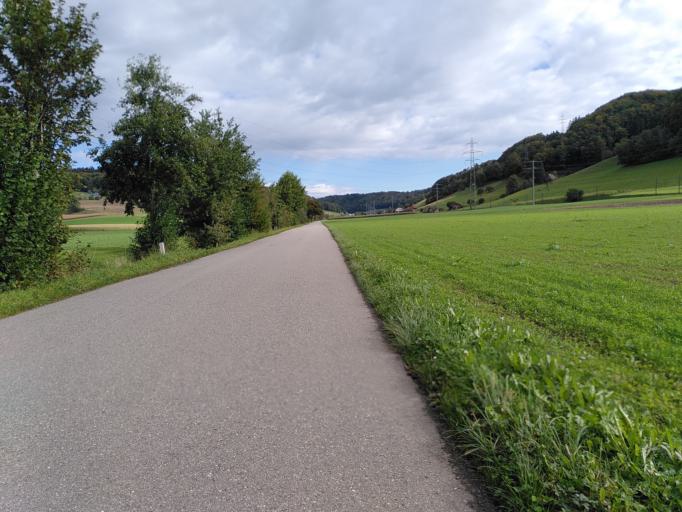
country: CH
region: Bern
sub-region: Oberaargau
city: Seeberg
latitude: 47.1268
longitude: 7.6746
